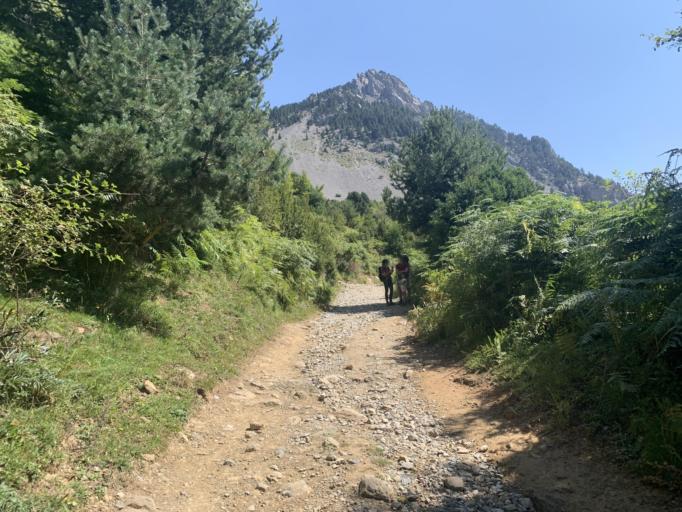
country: ES
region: Aragon
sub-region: Provincia de Huesca
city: Bielsa
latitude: 42.6844
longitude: 0.0833
